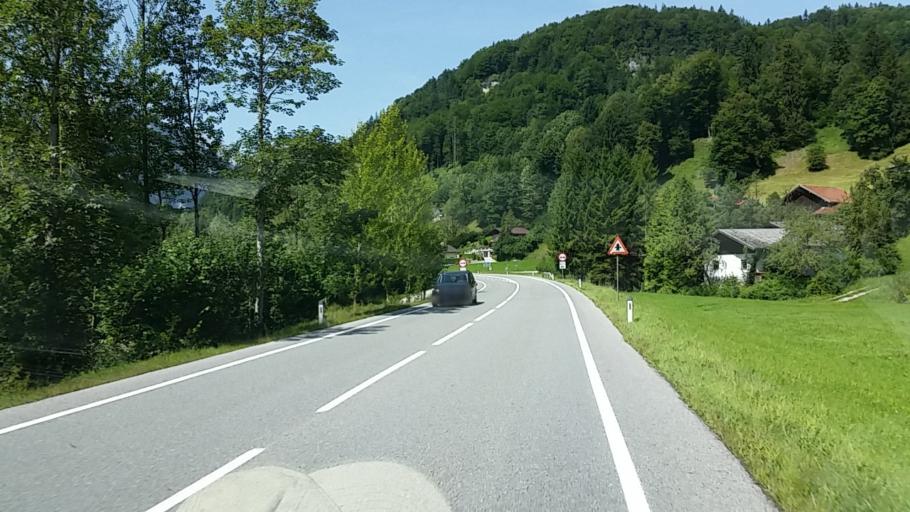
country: AT
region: Salzburg
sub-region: Politischer Bezirk Hallein
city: Scheffau am Tennengebirge
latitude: 47.5905
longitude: 13.2035
